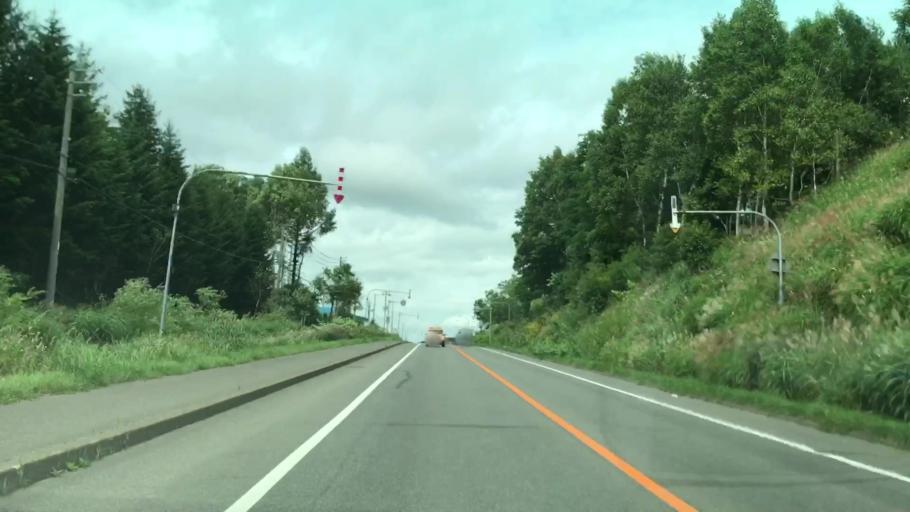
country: JP
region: Hokkaido
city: Niseko Town
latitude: 42.9130
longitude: 140.7521
